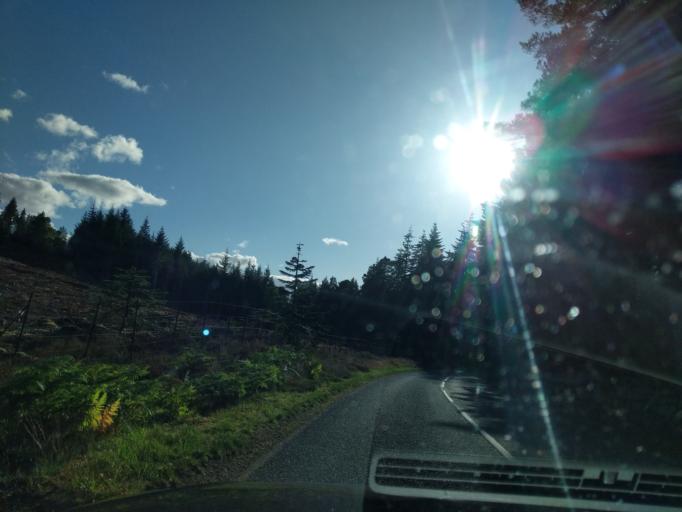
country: GB
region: Scotland
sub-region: Aberdeenshire
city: Aboyne
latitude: 57.0644
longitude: -2.8111
